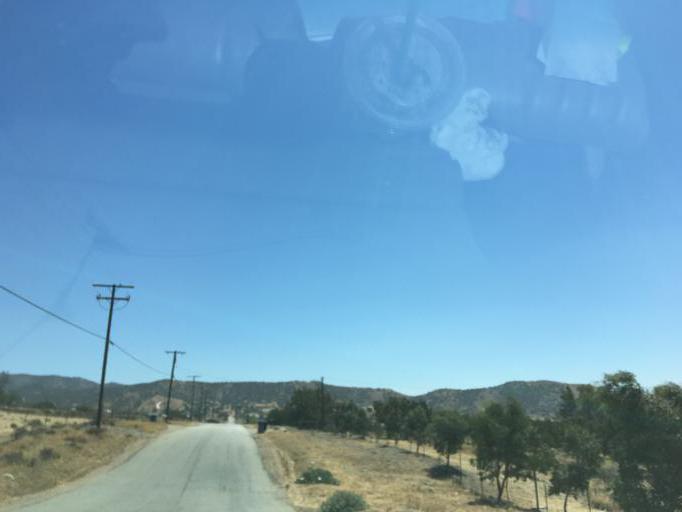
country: US
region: California
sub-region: Los Angeles County
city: Acton
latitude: 34.5246
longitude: -118.2356
